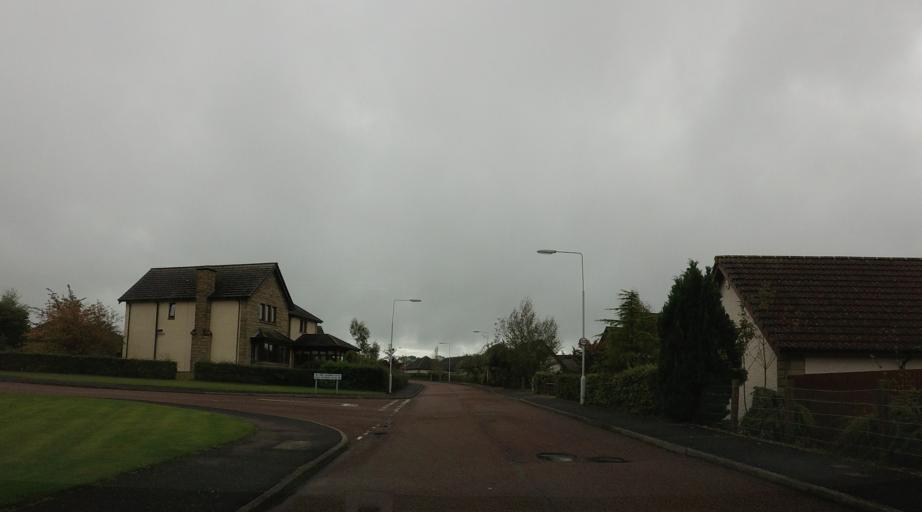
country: GB
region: Scotland
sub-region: Fife
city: Balmullo
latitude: 56.4093
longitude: -2.9107
